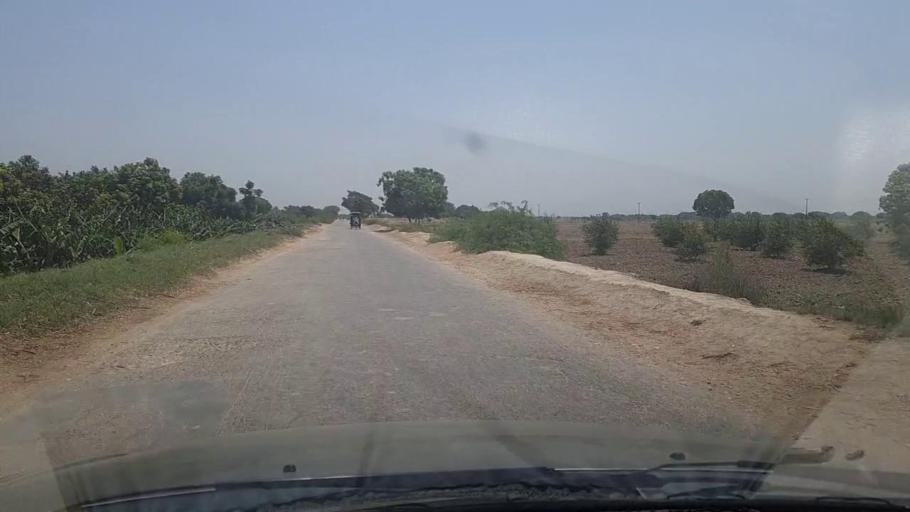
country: PK
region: Sindh
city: Tando Muhammad Khan
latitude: 25.2735
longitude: 68.6272
